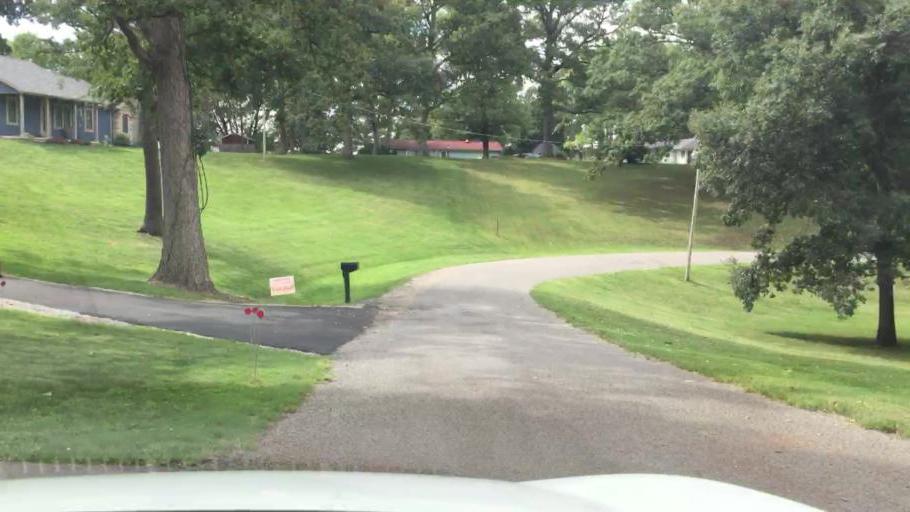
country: US
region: Ohio
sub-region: Champaign County
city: Urbana
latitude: 40.0966
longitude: -83.7043
